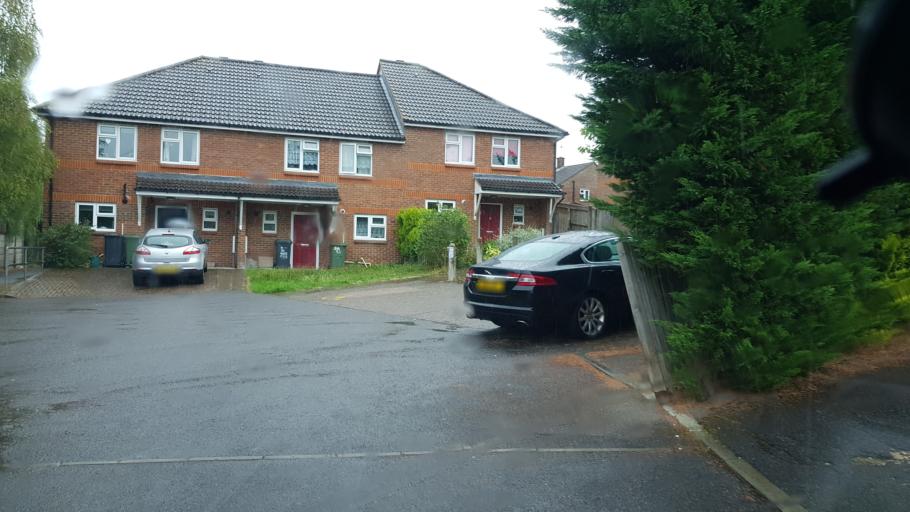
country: GB
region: England
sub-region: Surrey
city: Guildford
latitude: 51.2458
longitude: -0.6155
